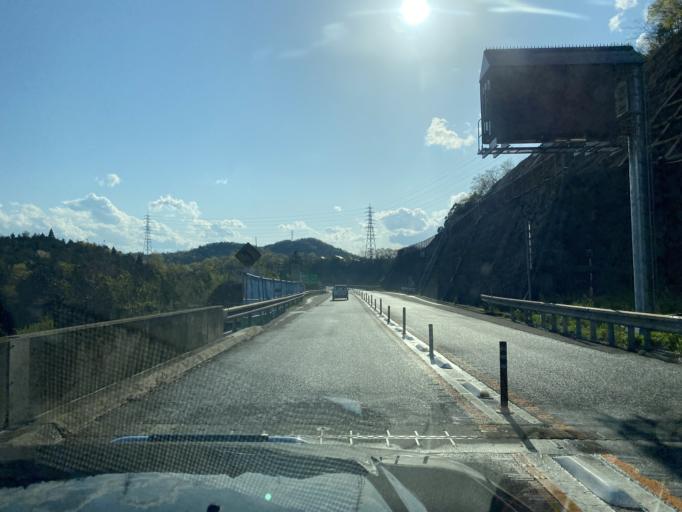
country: JP
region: Kyoto
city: Fukuchiyama
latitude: 35.2950
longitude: 135.1822
